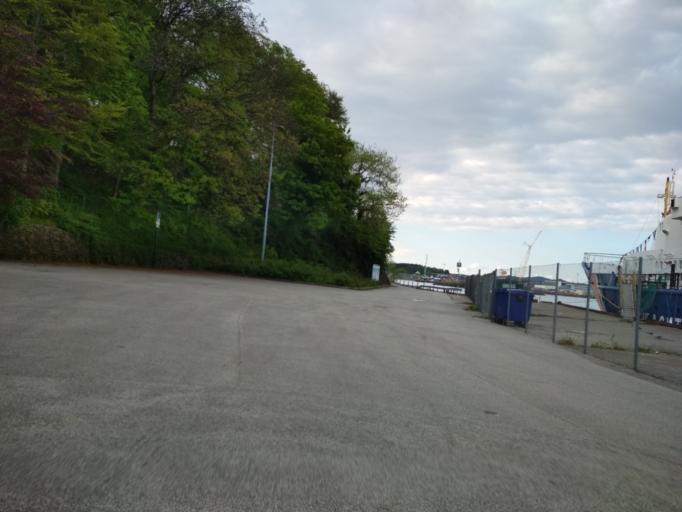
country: NO
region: Rogaland
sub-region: Stavanger
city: Stavanger
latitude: 58.9775
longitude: 5.7211
